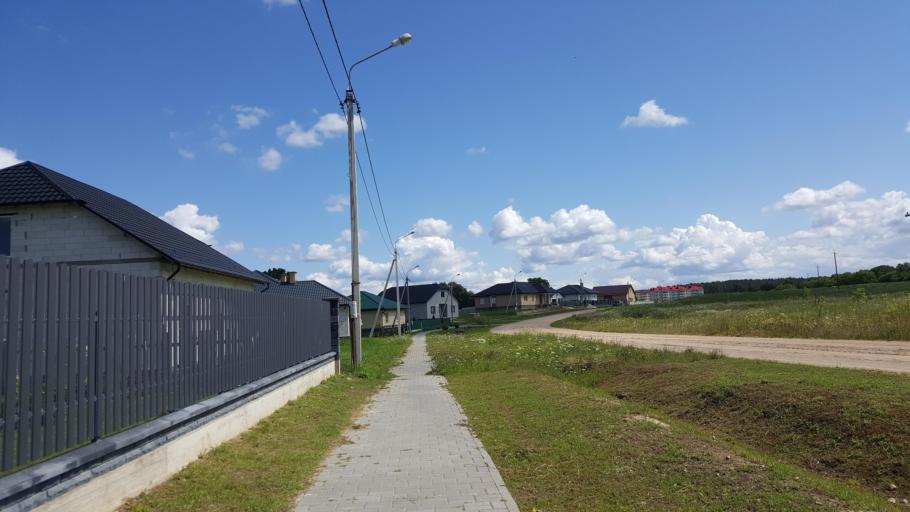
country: BY
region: Brest
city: Kamyanyets
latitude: 52.3850
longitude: 23.8067
